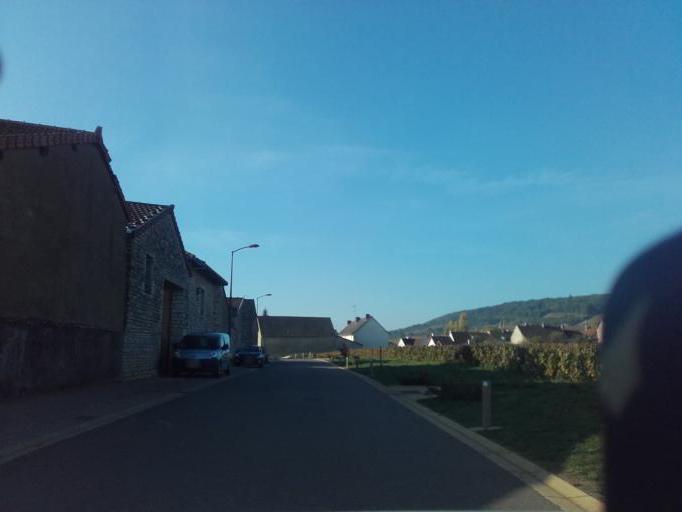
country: FR
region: Bourgogne
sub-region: Departement de la Cote-d'Or
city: Corpeau
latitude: 46.9394
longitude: 4.7345
